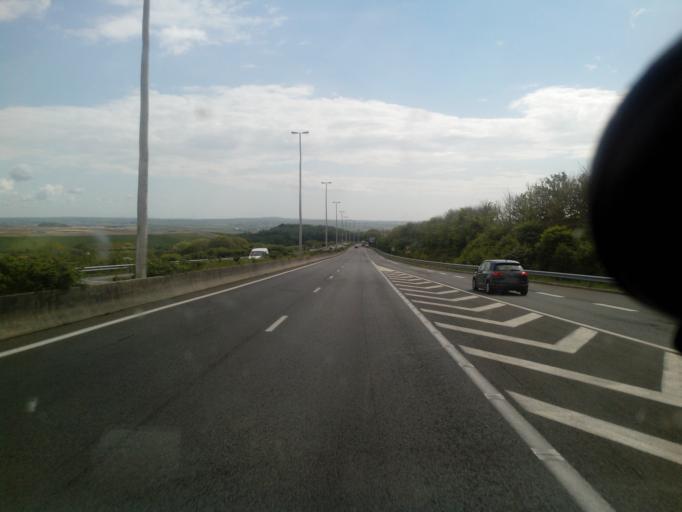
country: FR
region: Nord-Pas-de-Calais
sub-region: Departement du Pas-de-Calais
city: Ferques
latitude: 50.8582
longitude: 1.7320
